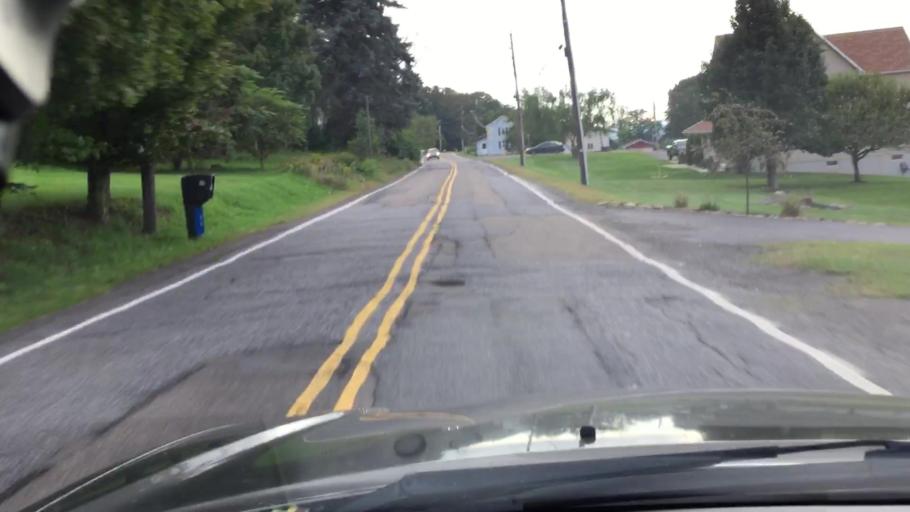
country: US
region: Pennsylvania
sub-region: Luzerne County
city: Harleigh
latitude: 41.0052
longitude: -75.9740
